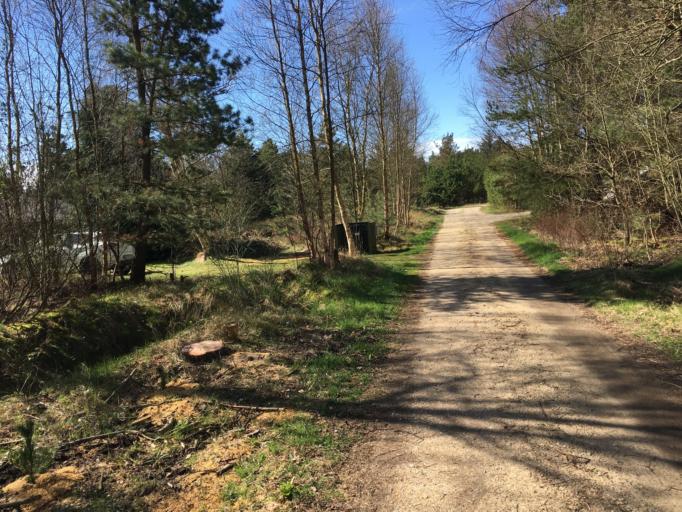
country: DK
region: South Denmark
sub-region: Varde Kommune
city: Oksbol
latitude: 55.5599
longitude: 8.2216
